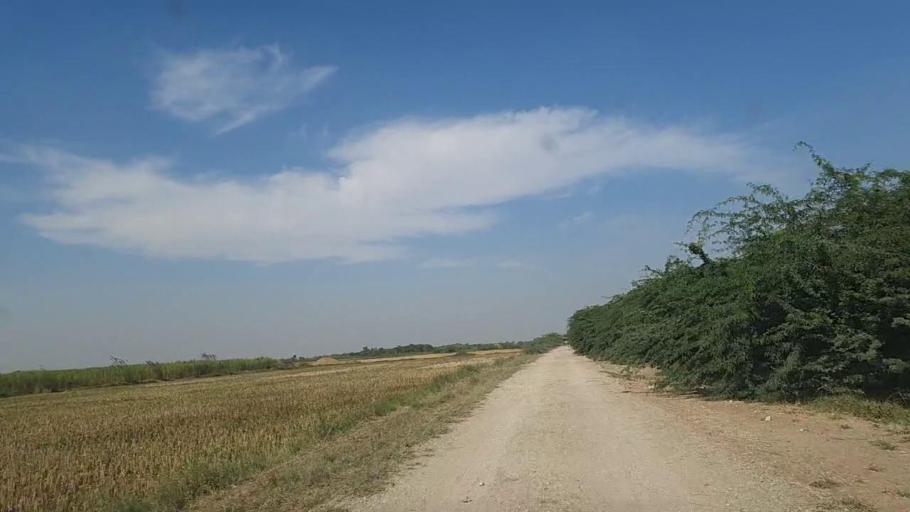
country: PK
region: Sindh
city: Bulri
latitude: 24.8332
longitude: 68.2727
